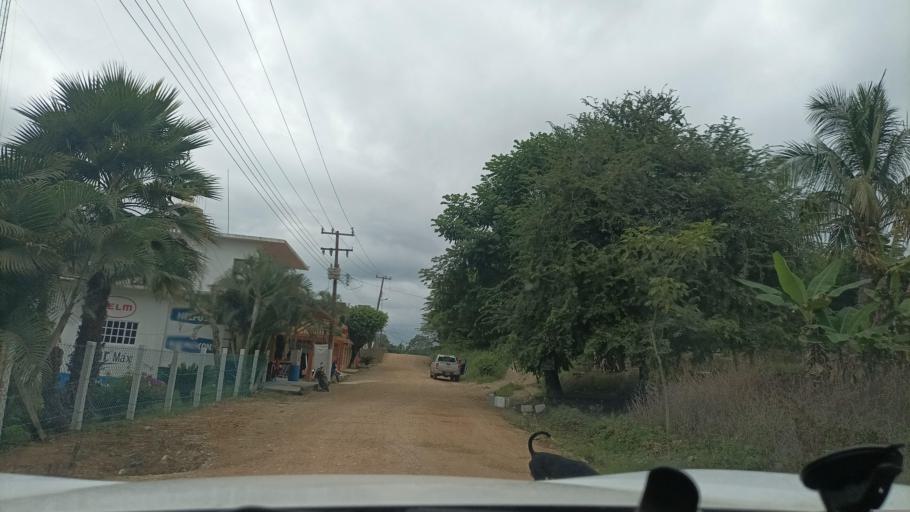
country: MX
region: Veracruz
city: Hidalgotitlan
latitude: 17.6389
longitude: -94.5117
